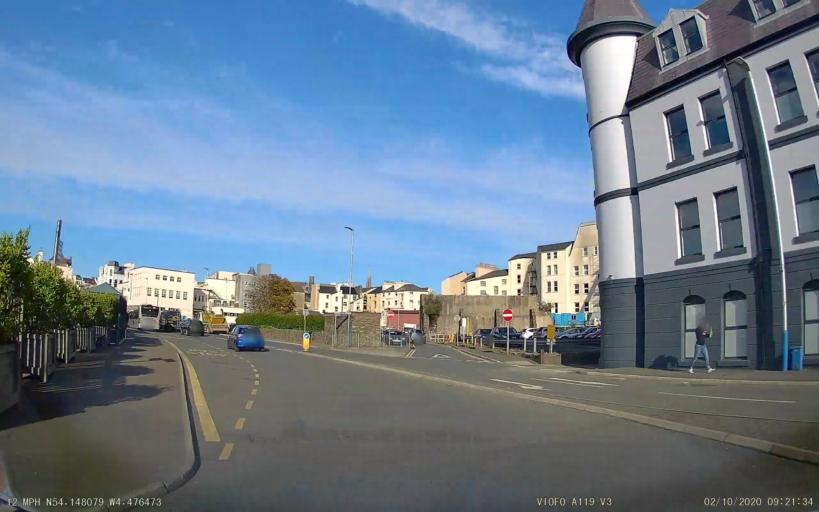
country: IM
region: Douglas
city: Douglas
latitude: 54.1482
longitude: -4.4766
